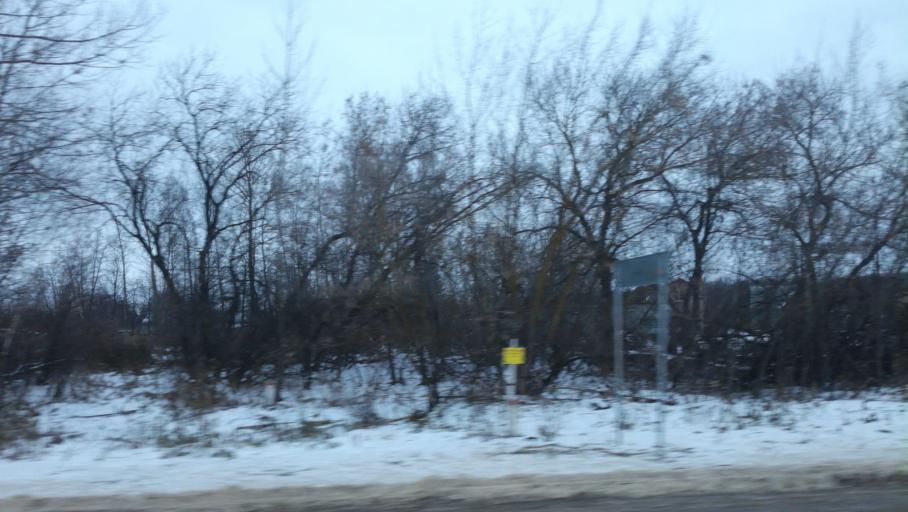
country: RU
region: Tula
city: Kosaya Gora
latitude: 54.1782
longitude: 37.5050
